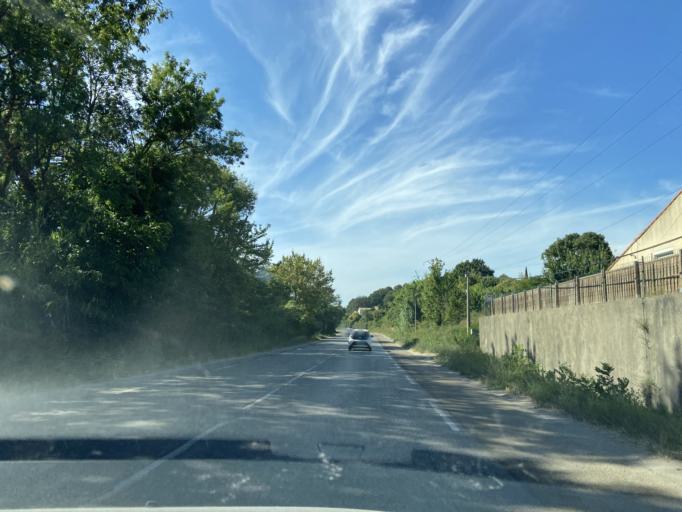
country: FR
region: Provence-Alpes-Cote d'Azur
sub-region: Departement des Bouches-du-Rhone
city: Saint-Chamas
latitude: 43.5605
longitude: 5.0306
